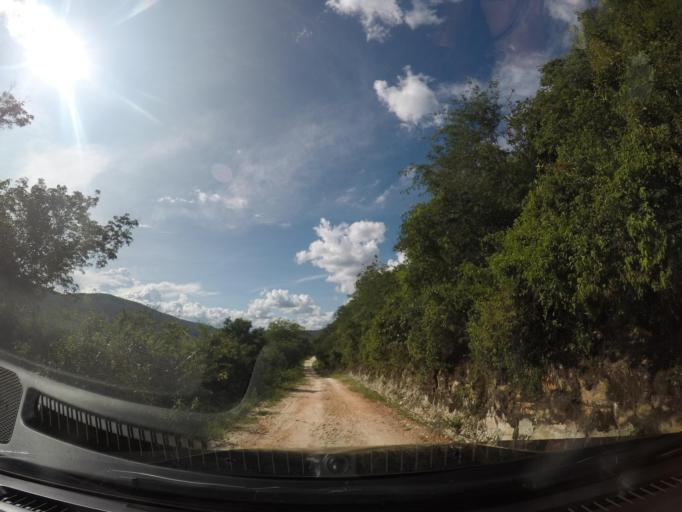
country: BR
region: Bahia
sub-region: Livramento Do Brumado
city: Livramento do Brumado
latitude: -13.2189
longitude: -41.6000
